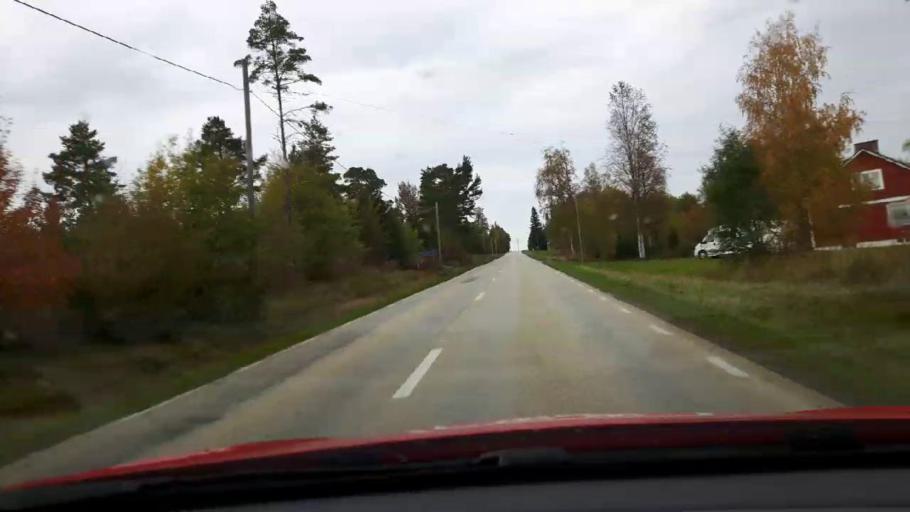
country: SE
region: Jaemtland
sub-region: Bergs Kommun
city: Hoverberg
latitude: 62.9831
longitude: 14.3426
